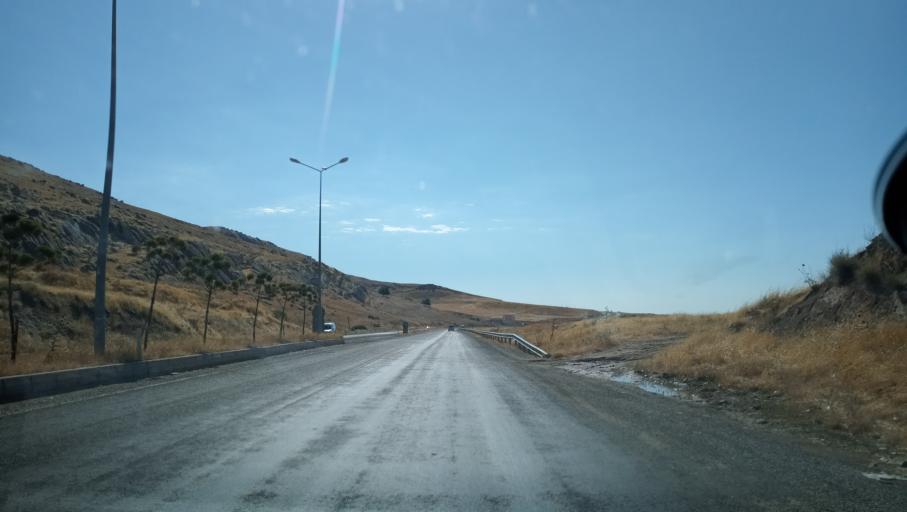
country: TR
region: Diyarbakir
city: Silvan
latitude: 38.1331
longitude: 41.0432
